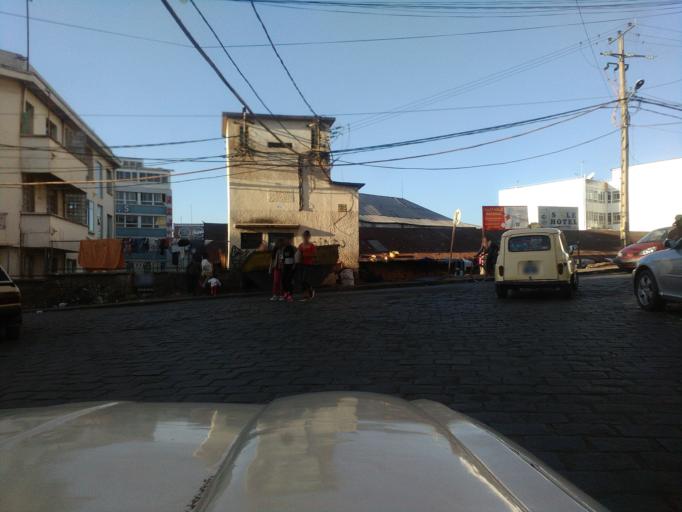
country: MG
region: Analamanga
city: Antananarivo
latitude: -18.9077
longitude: 47.5222
